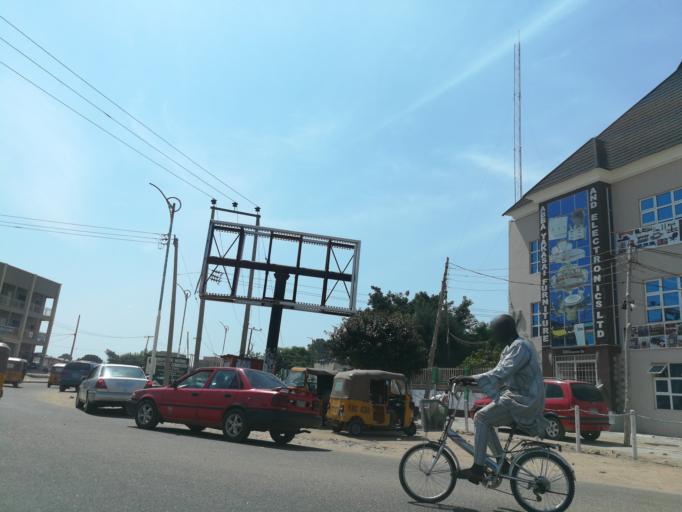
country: NG
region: Kano
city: Kano
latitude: 12.0285
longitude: 8.5229
